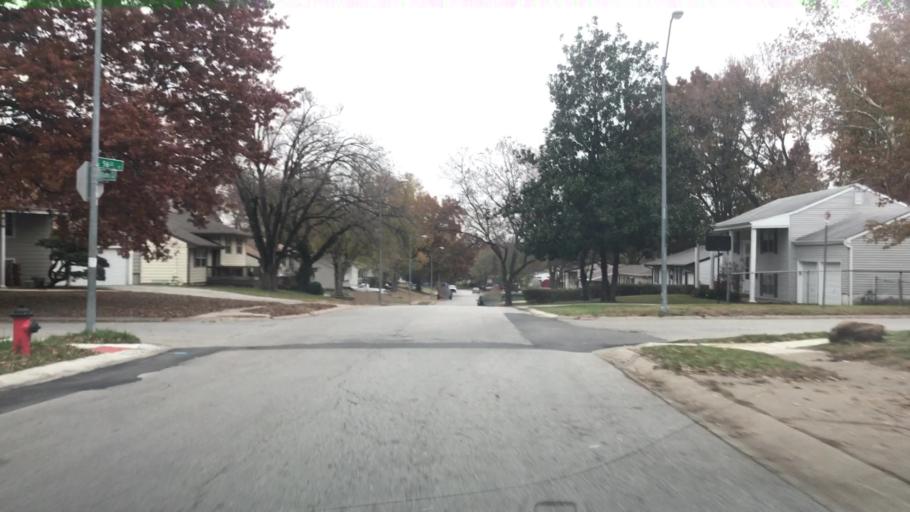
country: US
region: Missouri
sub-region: Clay County
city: Claycomo
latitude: 39.1946
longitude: -94.4865
